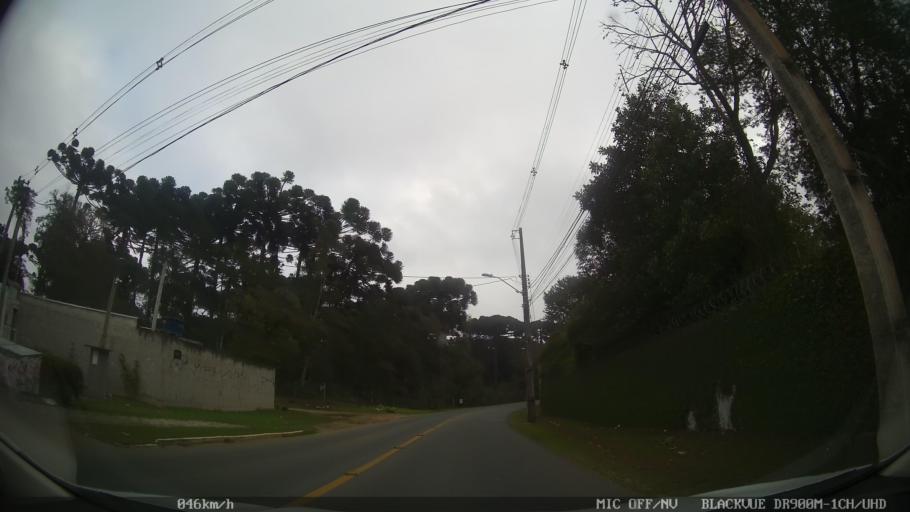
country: BR
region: Parana
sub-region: Curitiba
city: Curitiba
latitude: -25.3883
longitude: -49.3211
